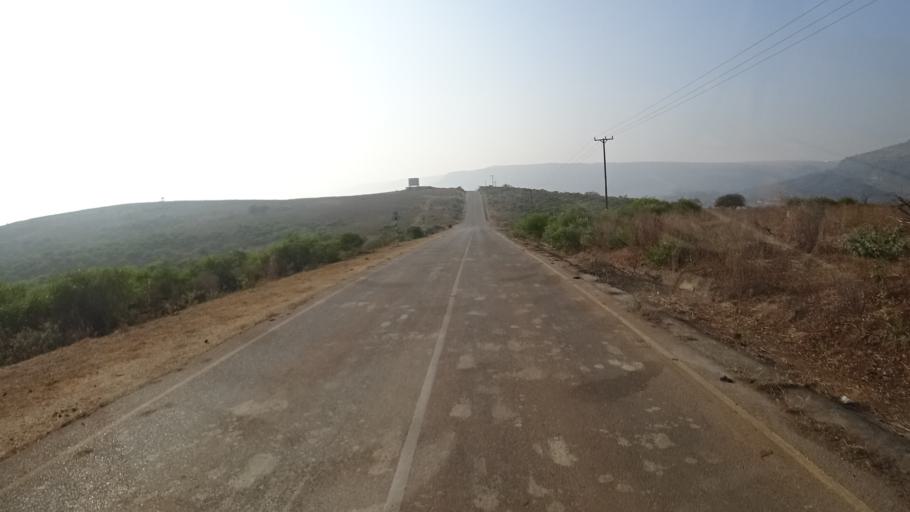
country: YE
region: Al Mahrah
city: Hawf
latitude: 16.7449
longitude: 53.3500
